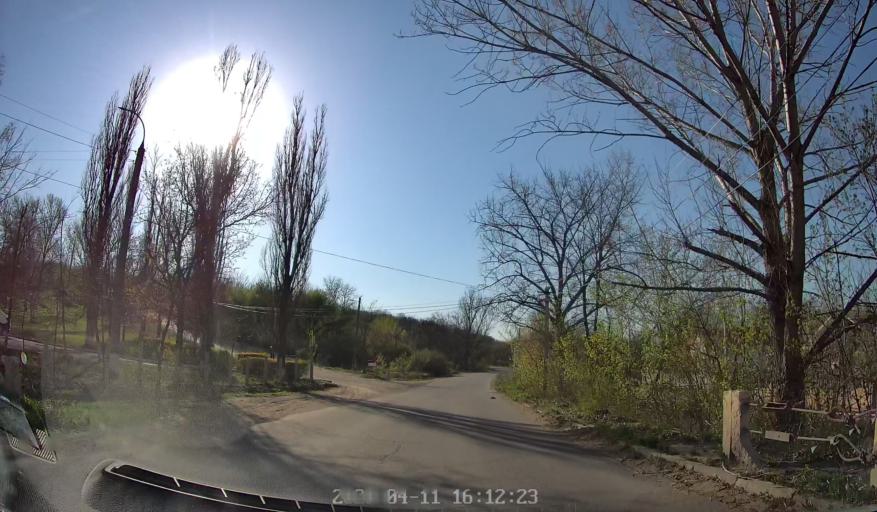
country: MD
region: Chisinau
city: Vadul lui Voda
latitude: 47.0695
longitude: 29.1223
